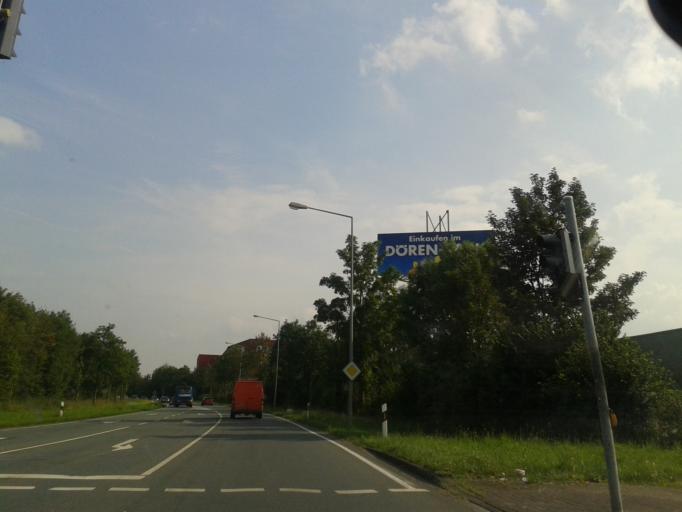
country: DE
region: North Rhine-Westphalia
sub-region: Regierungsbezirk Detmold
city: Paderborn
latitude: 51.7379
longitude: 8.7867
